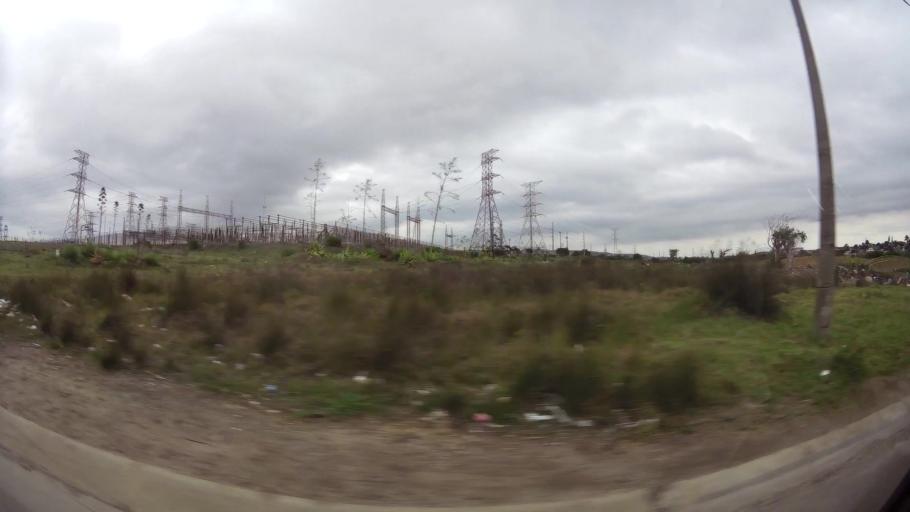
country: ZA
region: Eastern Cape
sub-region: Nelson Mandela Bay Metropolitan Municipality
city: Port Elizabeth
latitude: -33.9113
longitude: 25.5685
